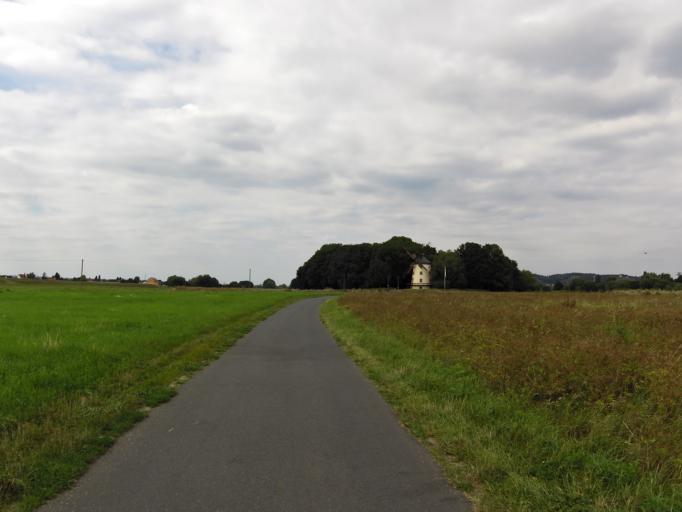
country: DE
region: Saxony
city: Radebeul
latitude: 51.0883
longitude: 13.6598
